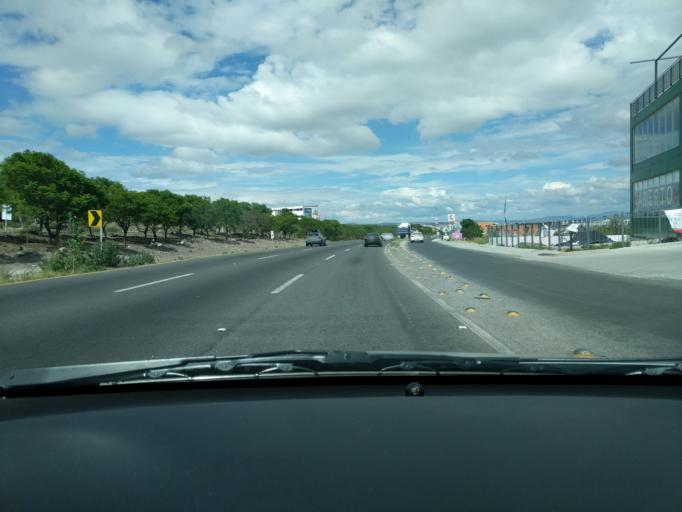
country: MX
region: Queretaro
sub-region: El Marques
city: La Pradera
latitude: 20.6611
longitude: -100.3488
